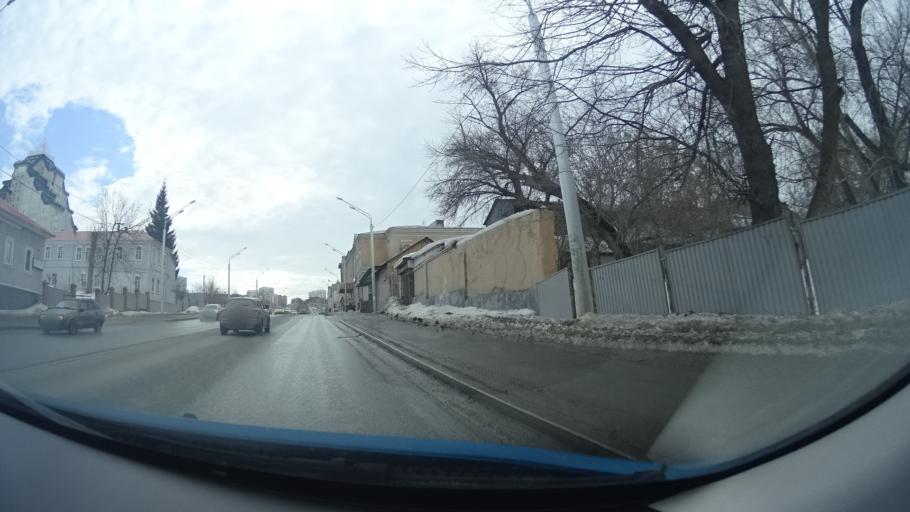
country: RU
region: Bashkortostan
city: Ufa
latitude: 54.7088
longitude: 55.9669
